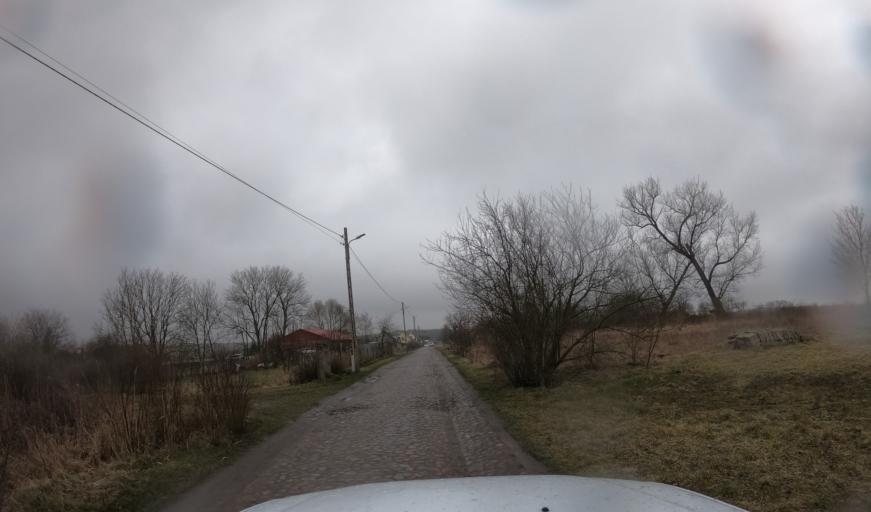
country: PL
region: West Pomeranian Voivodeship
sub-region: Powiat kamienski
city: Kamien Pomorski
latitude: 53.8927
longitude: 14.8272
